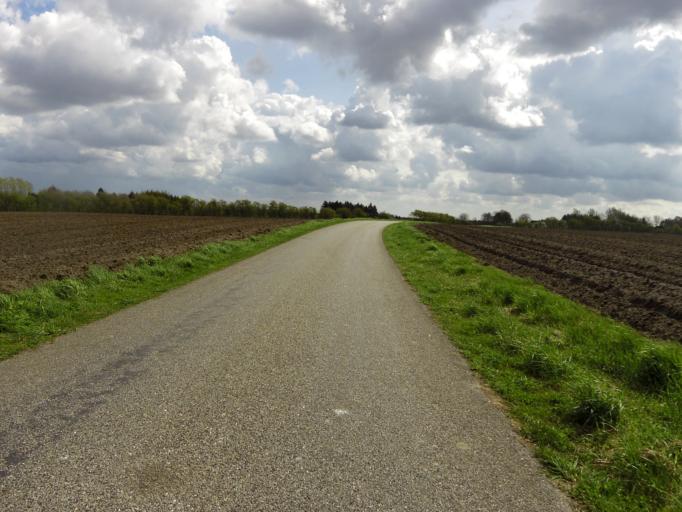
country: DK
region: South Denmark
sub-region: Tonder Kommune
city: Toftlund
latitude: 55.2080
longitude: 9.1626
